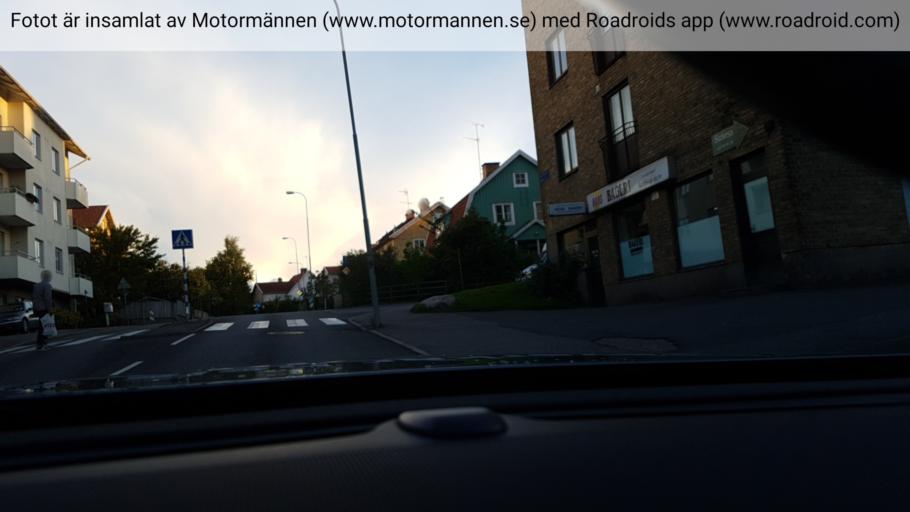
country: SE
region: Vaestra Goetaland
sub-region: Molndal
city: Moelndal
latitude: 57.6799
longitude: 11.9941
